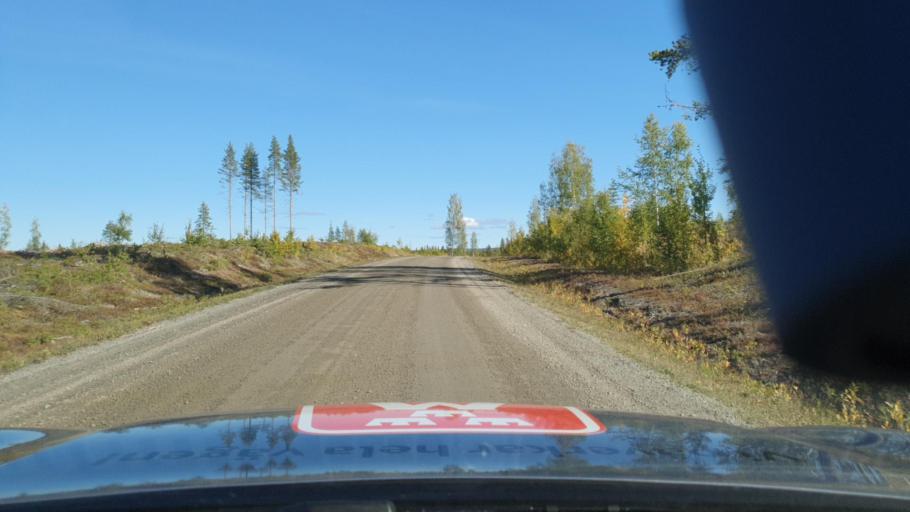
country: SE
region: Norrbotten
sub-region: Bodens Kommun
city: Boden
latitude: 66.0592
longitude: 21.3216
